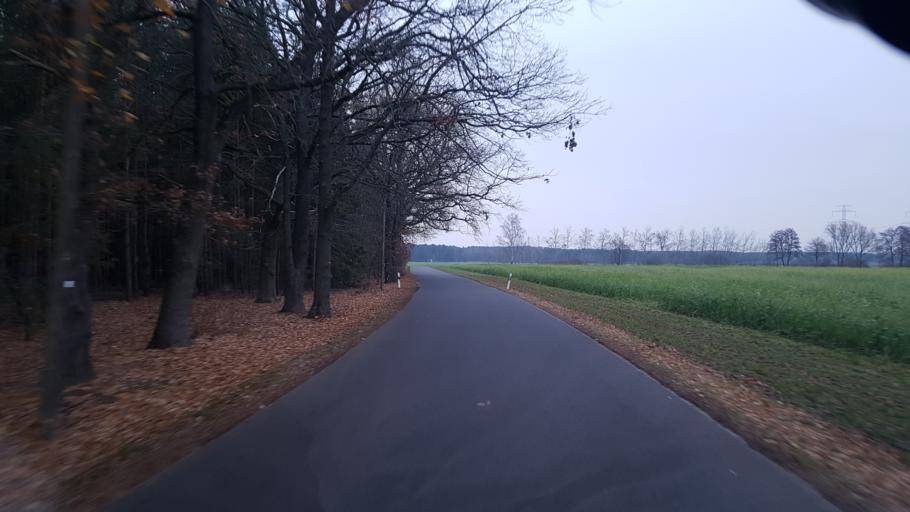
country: DE
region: Brandenburg
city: Peitz
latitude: 51.8833
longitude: 14.4007
